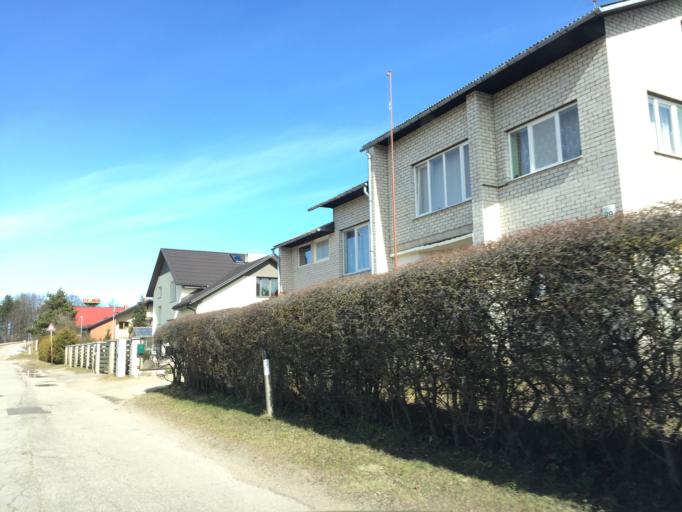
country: LV
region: Sigulda
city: Sigulda
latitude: 57.1392
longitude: 24.8227
